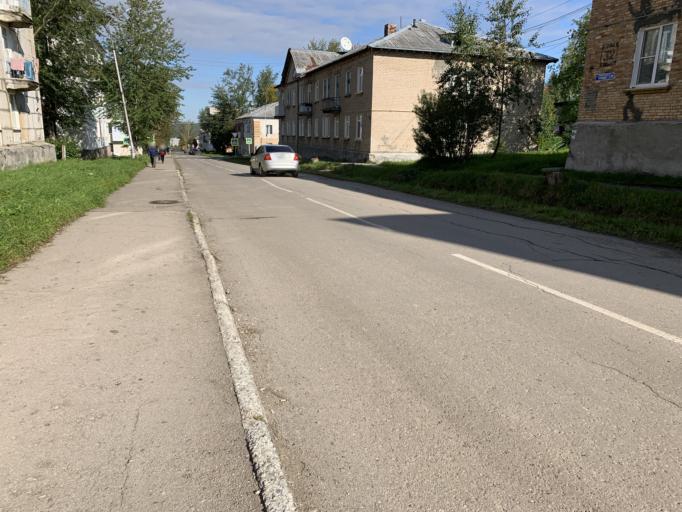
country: RU
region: Perm
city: Gubakha
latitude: 58.8398
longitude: 57.5555
